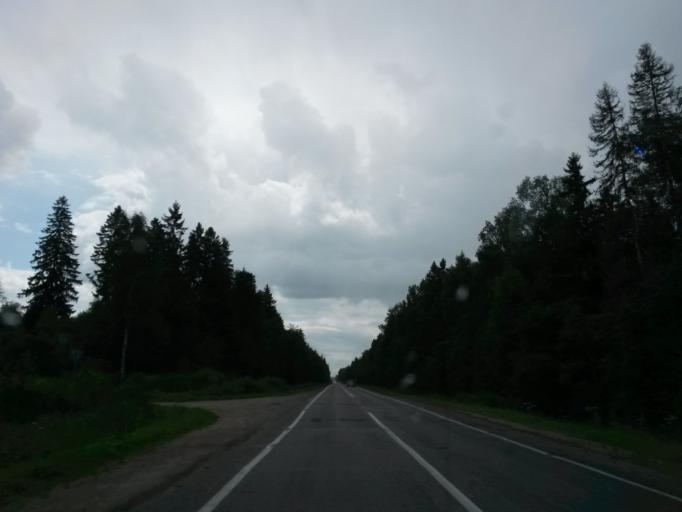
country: RU
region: Jaroslavl
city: Gavrilov-Yam
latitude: 57.4313
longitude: 39.9183
